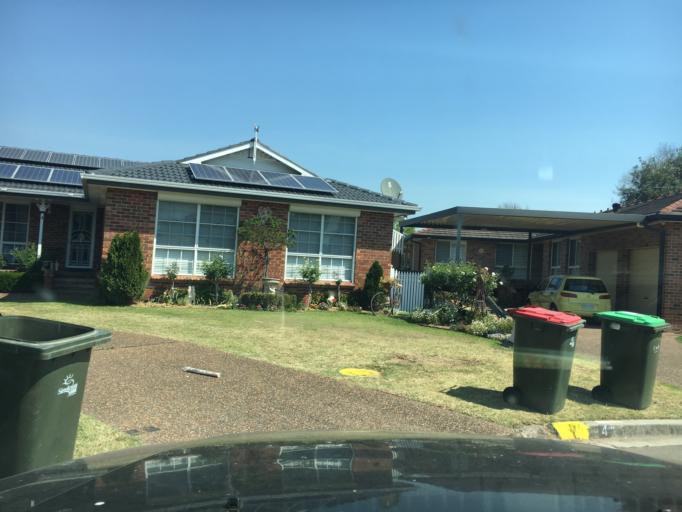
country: AU
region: New South Wales
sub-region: Singleton
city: Singleton
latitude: -32.5692
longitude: 151.1888
